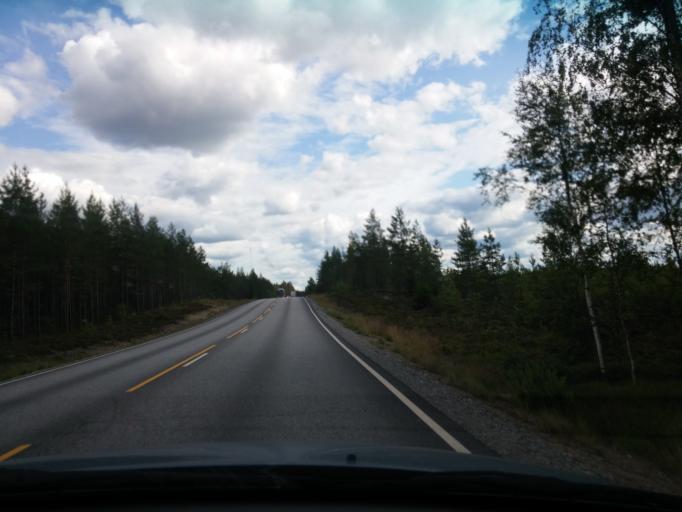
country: FI
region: Central Finland
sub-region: Keuruu
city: Multia
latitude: 62.5131
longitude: 24.6681
